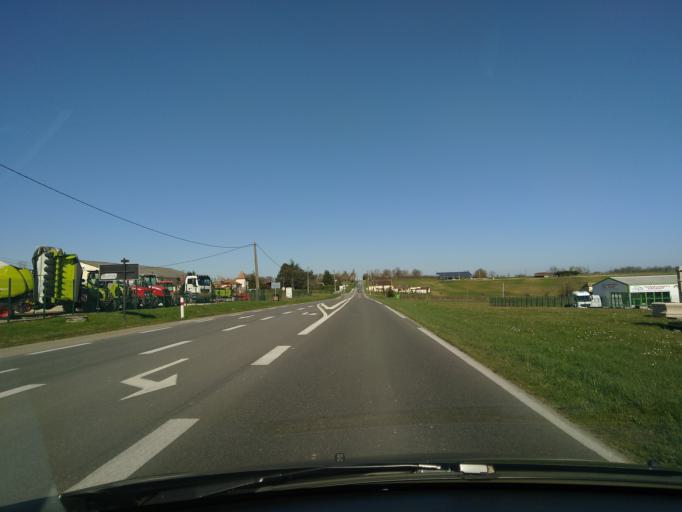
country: FR
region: Aquitaine
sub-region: Departement du Lot-et-Garonne
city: Cancon
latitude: 44.5463
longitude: 0.6256
